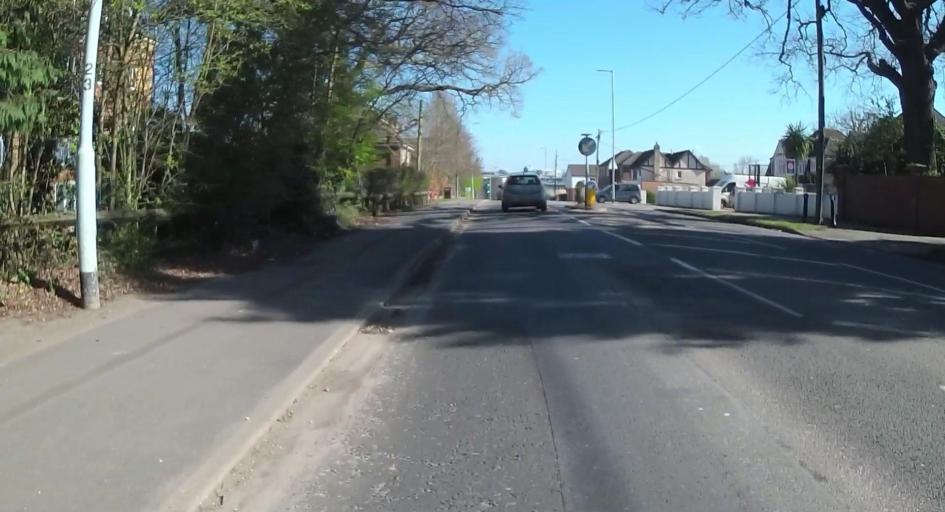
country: GB
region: England
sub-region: Bracknell Forest
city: Binfield
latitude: 51.4198
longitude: -0.7719
